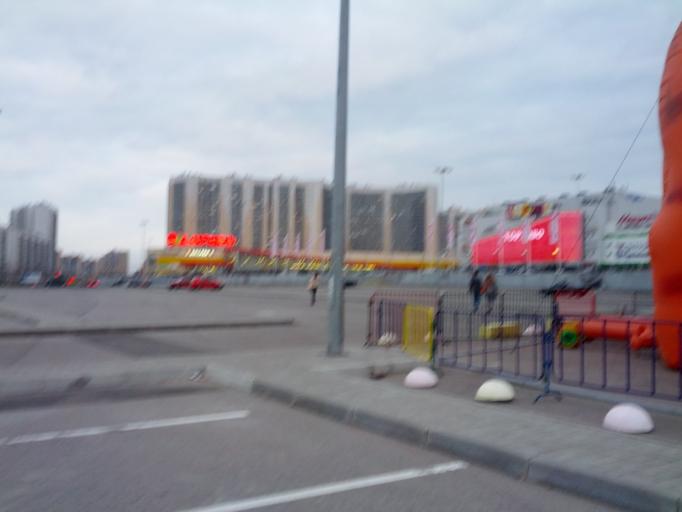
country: RU
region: St.-Petersburg
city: Obukhovo
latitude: 59.9122
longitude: 30.4415
